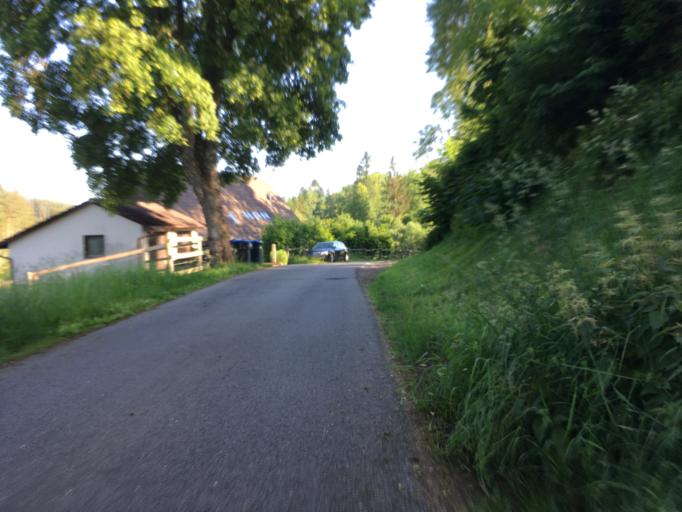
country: DE
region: Baden-Wuerttemberg
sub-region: Freiburg Region
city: Friedenweiler
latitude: 47.9231
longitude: 8.2556
